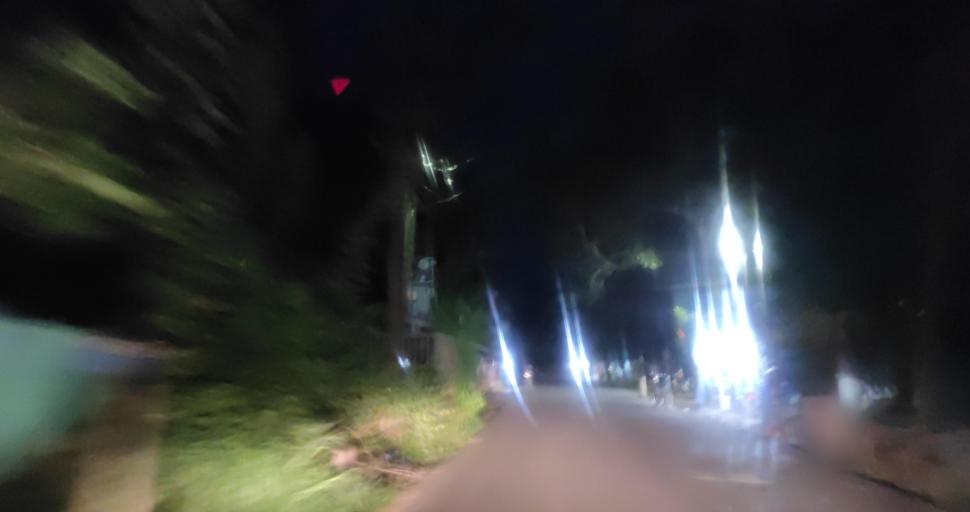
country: IN
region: Kerala
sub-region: Alappuzha
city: Vayalar
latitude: 9.6808
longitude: 76.3032
